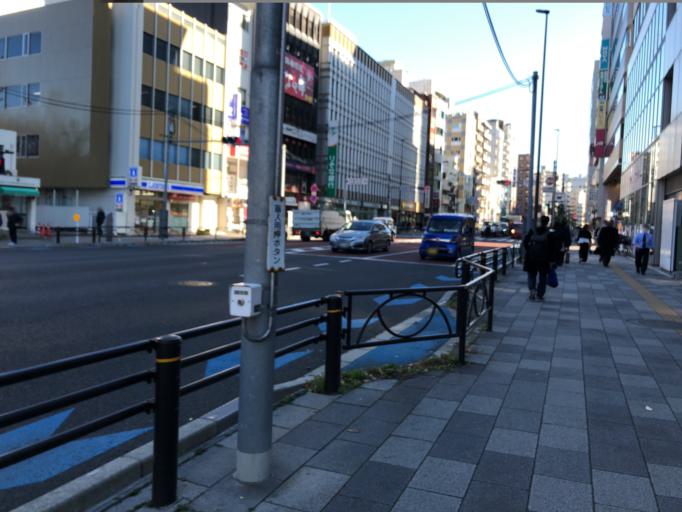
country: JP
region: Tokyo
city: Tokyo
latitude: 35.7180
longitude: 139.7363
